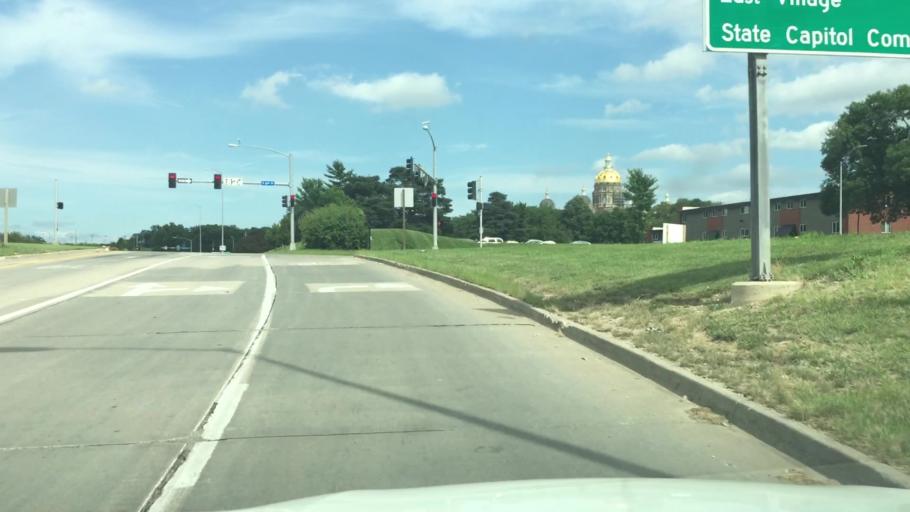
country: US
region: Iowa
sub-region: Polk County
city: Des Moines
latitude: 41.5946
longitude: -93.6116
